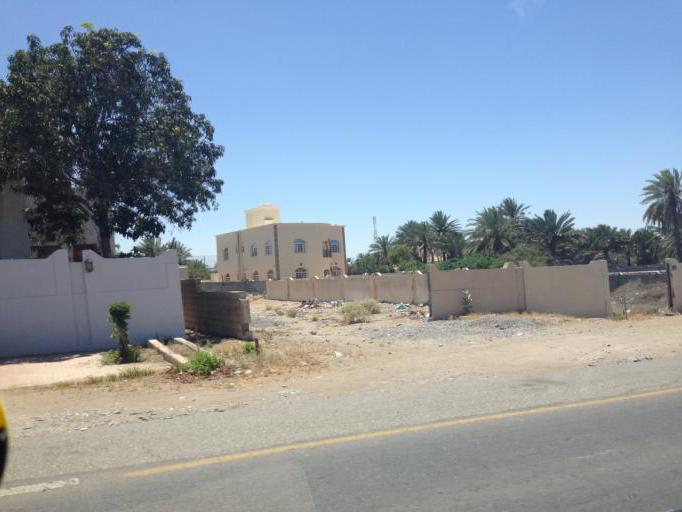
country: OM
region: Muhafazat Masqat
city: As Sib al Jadidah
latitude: 23.6628
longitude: 58.2091
